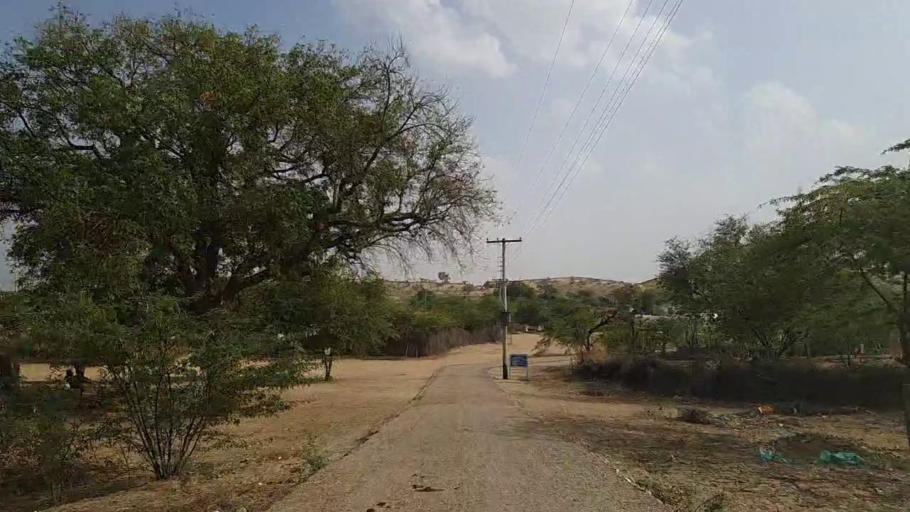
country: PK
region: Sindh
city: Islamkot
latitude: 24.8707
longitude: 70.1663
